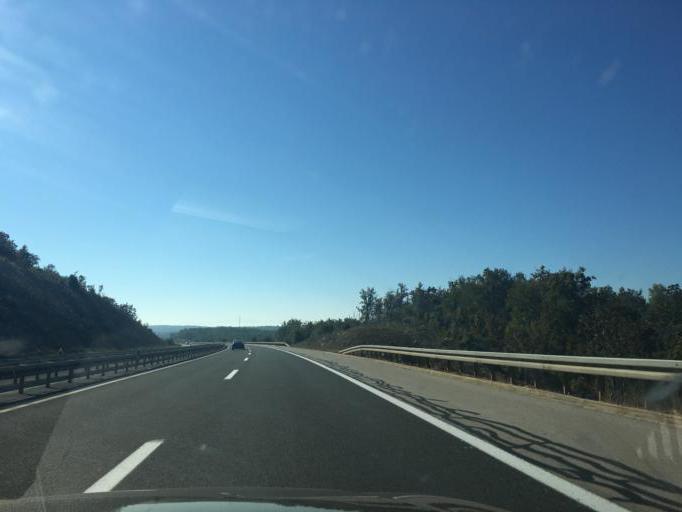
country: HR
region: Licko-Senjska
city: Otocac
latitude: 44.7398
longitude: 15.3785
